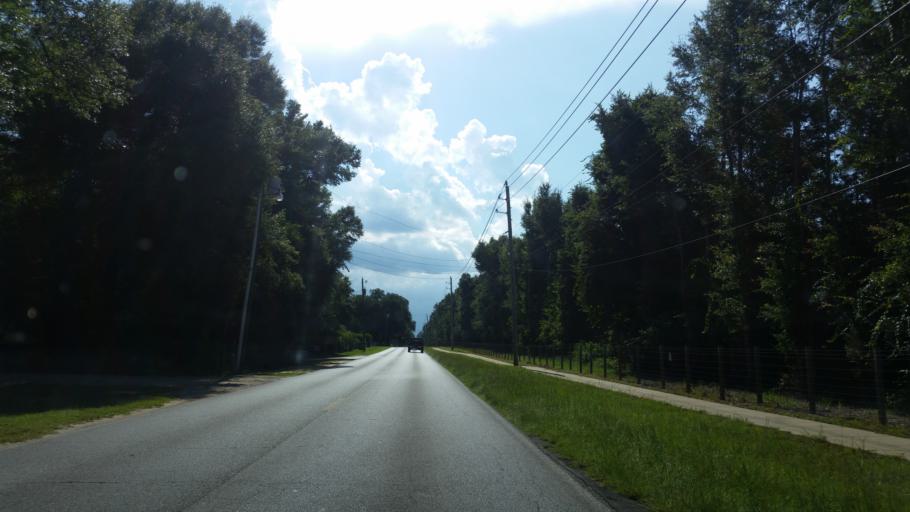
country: US
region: Florida
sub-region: Santa Rosa County
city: Pace
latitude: 30.6181
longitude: -87.1349
